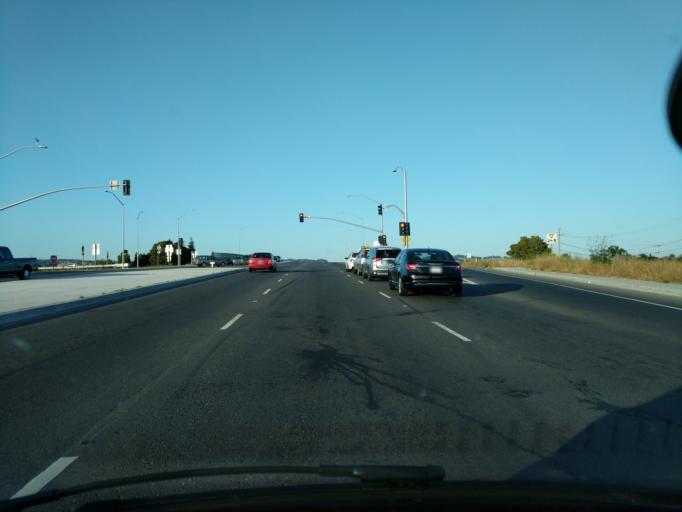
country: US
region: California
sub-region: Alameda County
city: San Leandro
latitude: 37.7186
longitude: -122.1787
